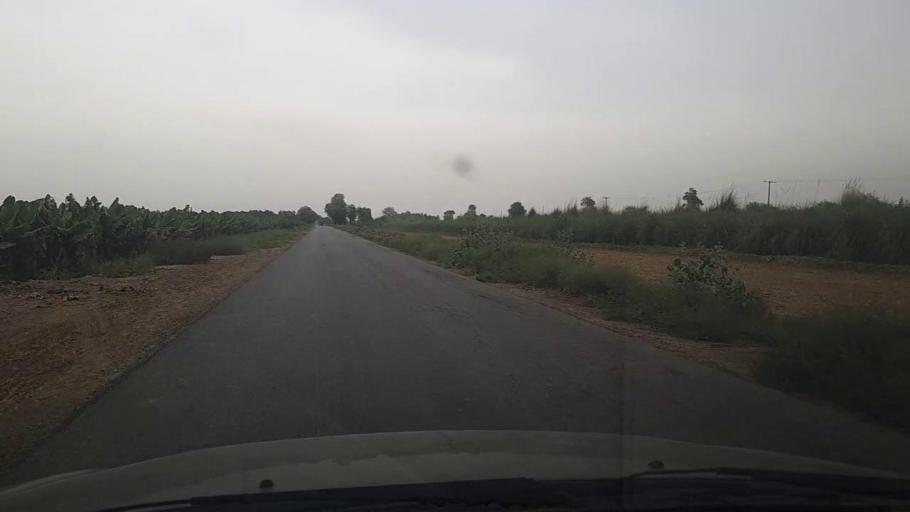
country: PK
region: Sindh
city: Daur
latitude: 26.3948
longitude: 68.2060
